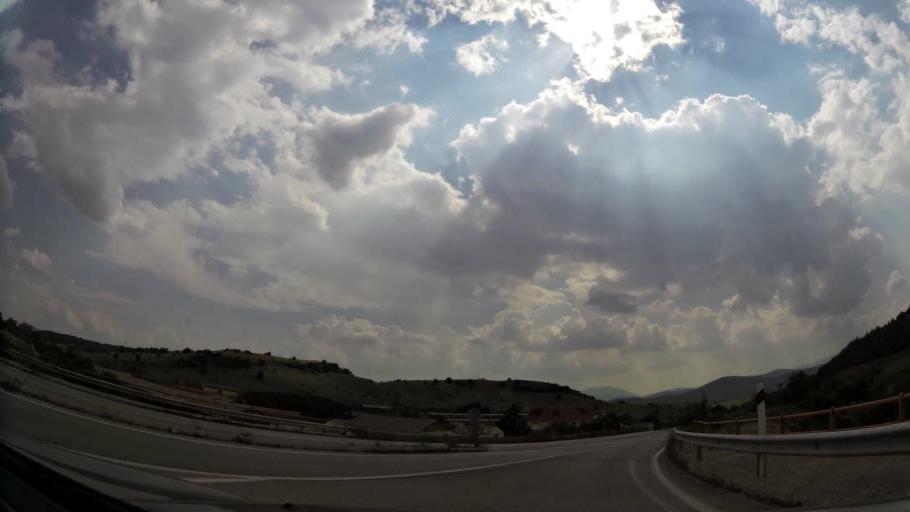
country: GR
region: West Macedonia
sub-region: Nomos Kozanis
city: Koila
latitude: 40.3422
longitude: 21.8240
